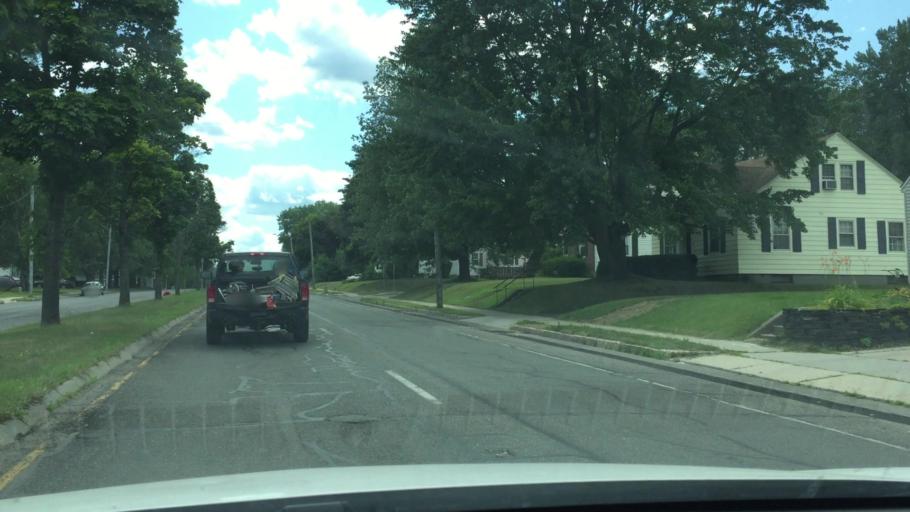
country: US
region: Massachusetts
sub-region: Berkshire County
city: Pittsfield
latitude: 42.4628
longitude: -73.2159
